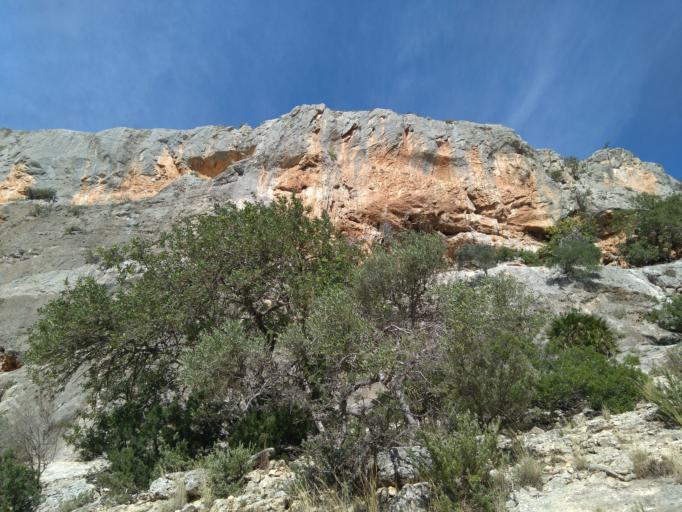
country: ES
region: Valencia
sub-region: Provincia de Valencia
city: Sumacarcer
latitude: 39.1606
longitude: -0.6594
